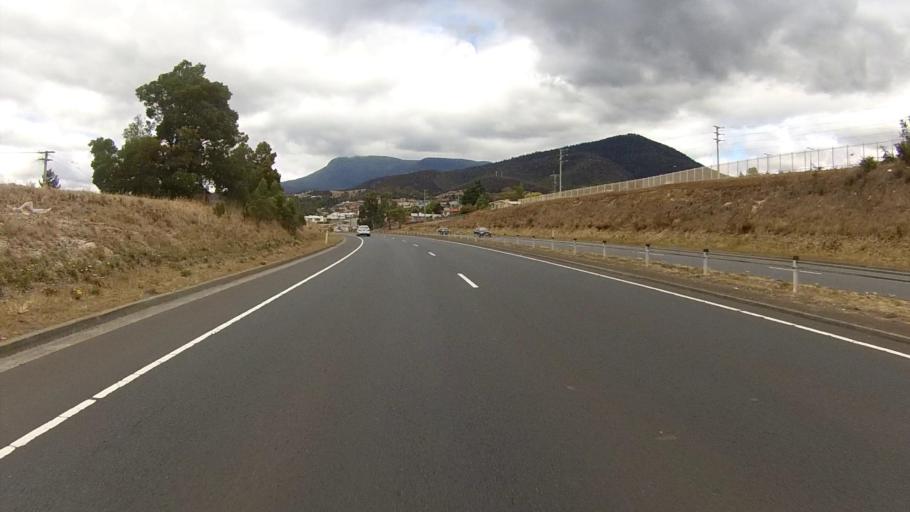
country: AU
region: Tasmania
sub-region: Glenorchy
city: Berriedale
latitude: -42.8059
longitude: 147.2491
